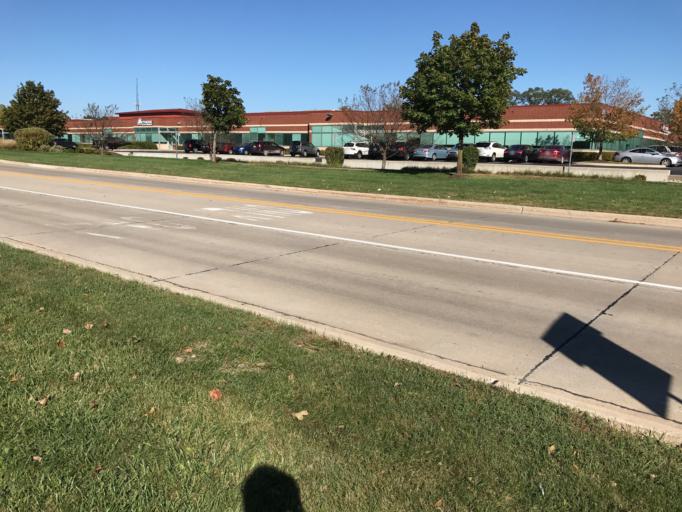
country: US
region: Michigan
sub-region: Oakland County
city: Franklin
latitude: 42.4864
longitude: -83.2966
